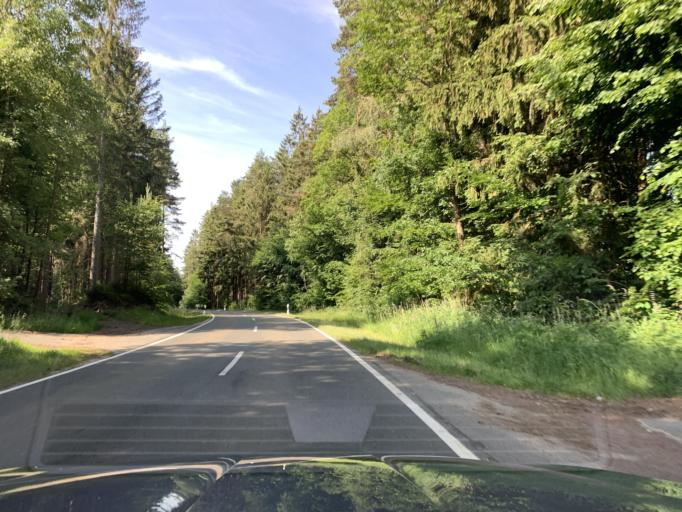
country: DE
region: Bavaria
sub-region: Upper Palatinate
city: Dieterskirchen
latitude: 49.4299
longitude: 12.4161
